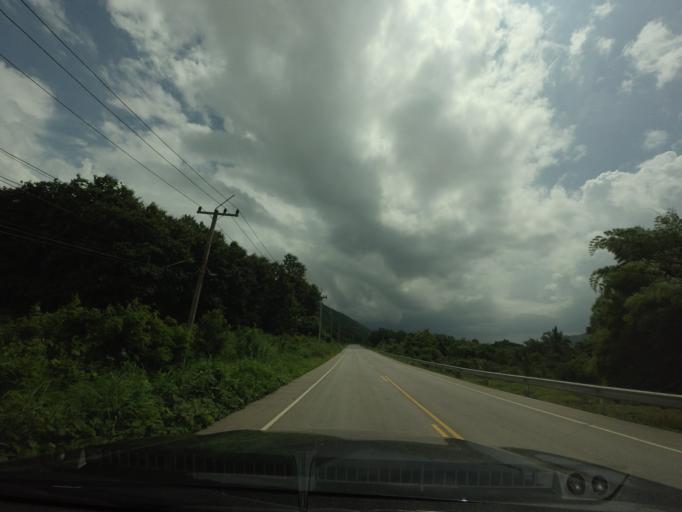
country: TH
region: Loei
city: Pak Chom
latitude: 18.0297
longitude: 101.7658
